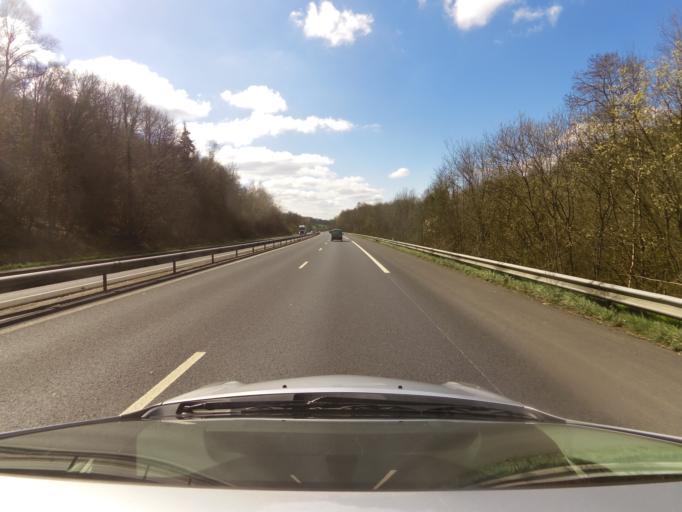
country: FR
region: Haute-Normandie
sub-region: Departement de la Seine-Maritime
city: Saint-Saens
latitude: 49.6700
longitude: 1.3162
